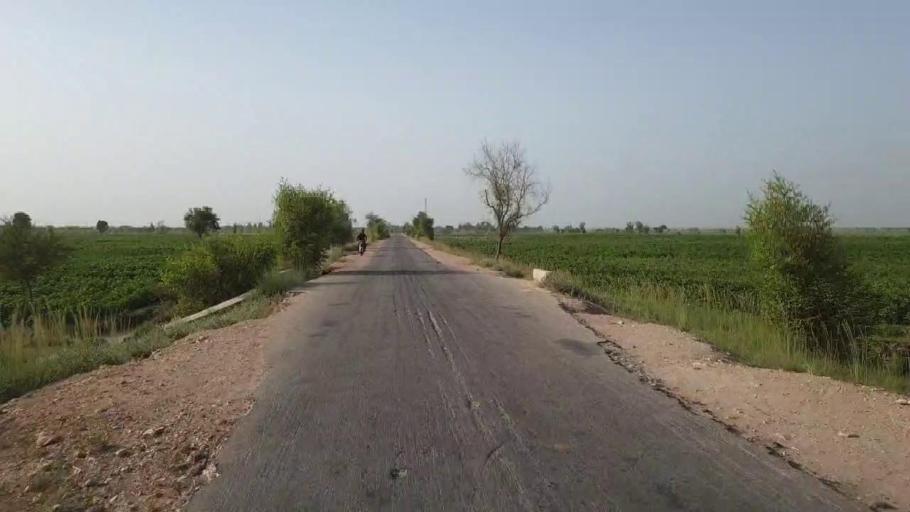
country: PK
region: Sindh
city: Jam Sahib
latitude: 26.4724
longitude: 68.8595
